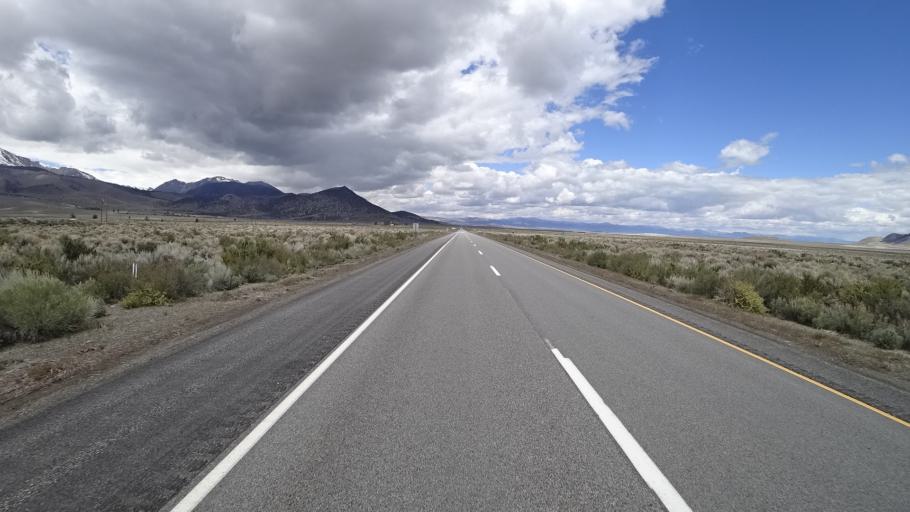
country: US
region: California
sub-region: Mono County
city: Mammoth Lakes
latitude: 37.8798
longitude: -119.0900
